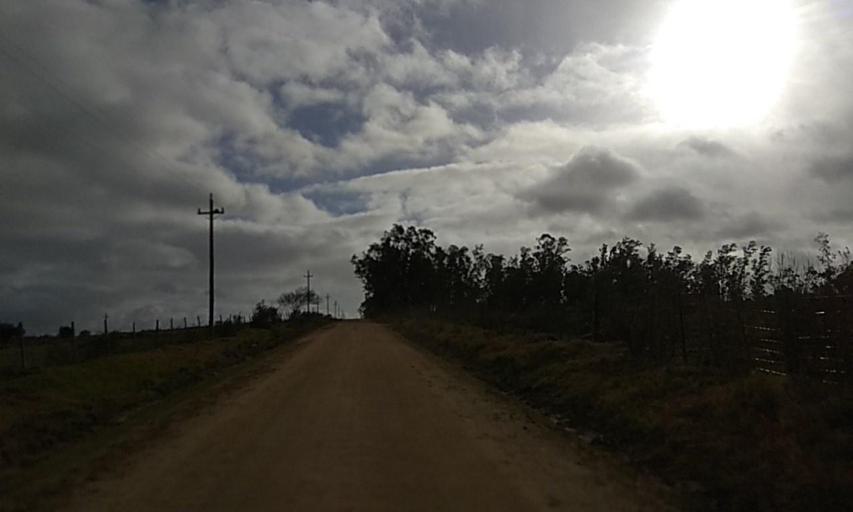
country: UY
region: Florida
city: Florida
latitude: -34.0588
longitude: -56.2286
